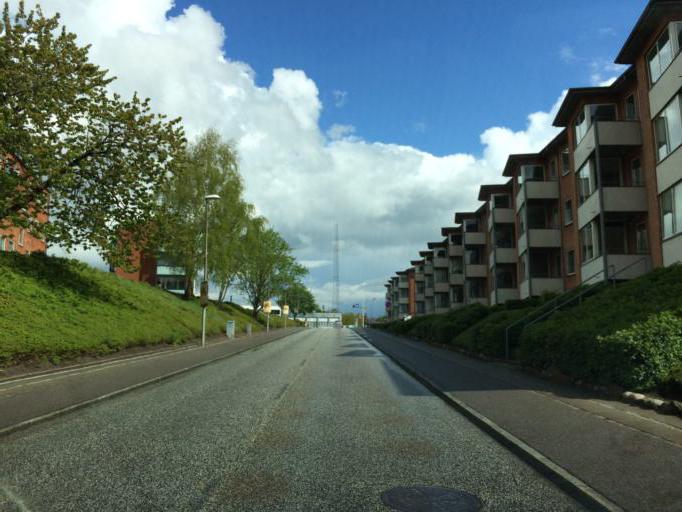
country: DK
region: Central Jutland
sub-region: Holstebro Kommune
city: Holstebro
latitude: 56.3586
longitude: 8.6095
